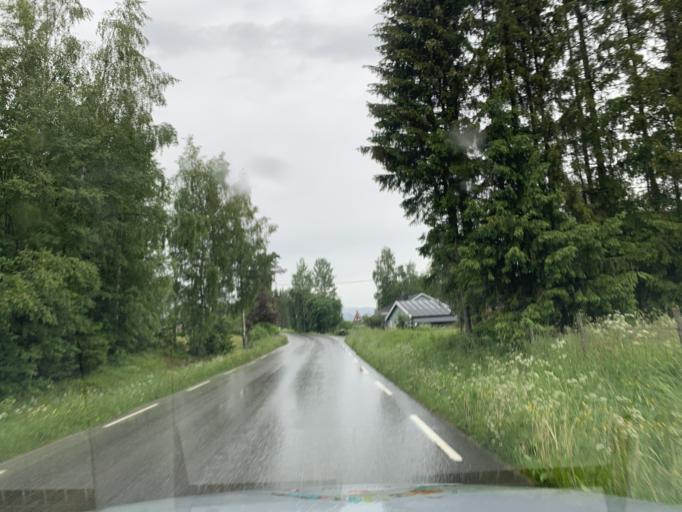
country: NO
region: Oppland
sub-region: Ringebu
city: Ringebu
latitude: 61.4470
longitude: 10.1798
